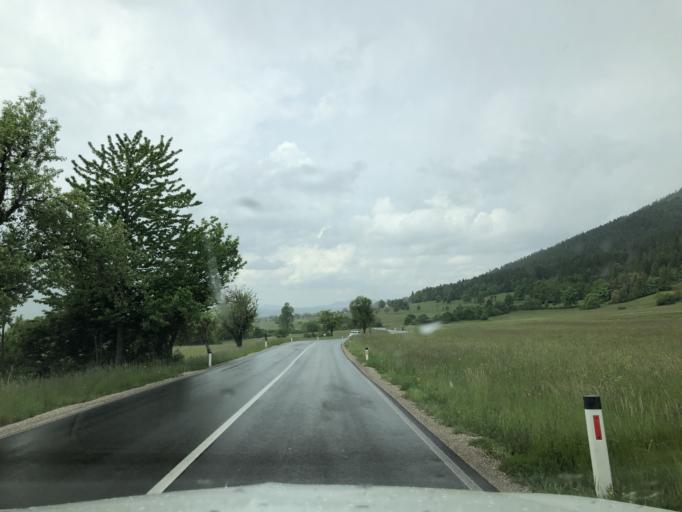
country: SI
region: Cerknica
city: Cerknica
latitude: 45.7719
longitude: 14.4185
